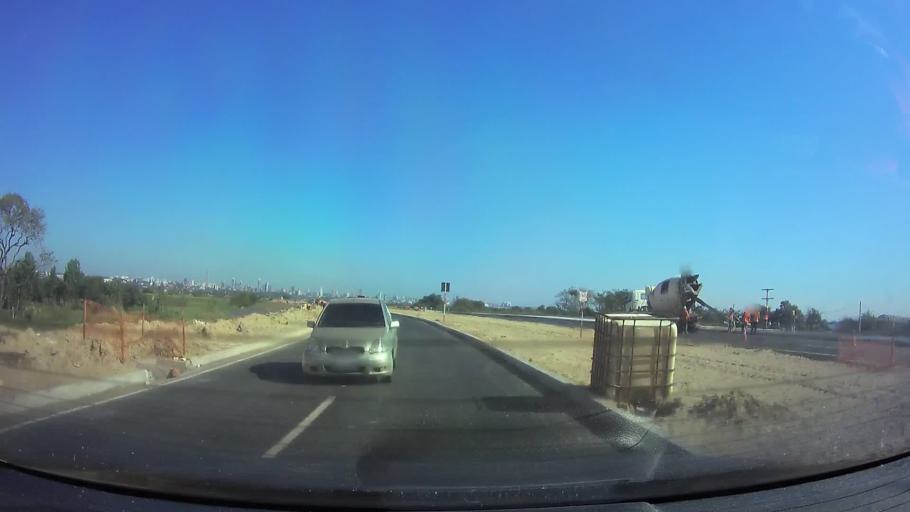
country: PY
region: Asuncion
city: Asuncion
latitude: -25.2504
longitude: -57.6042
